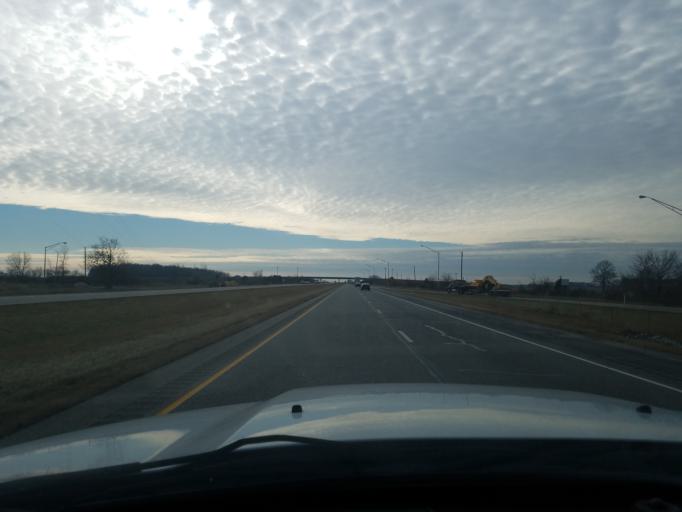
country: US
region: Indiana
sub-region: Huntington County
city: Warren
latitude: 40.7465
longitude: -85.4085
